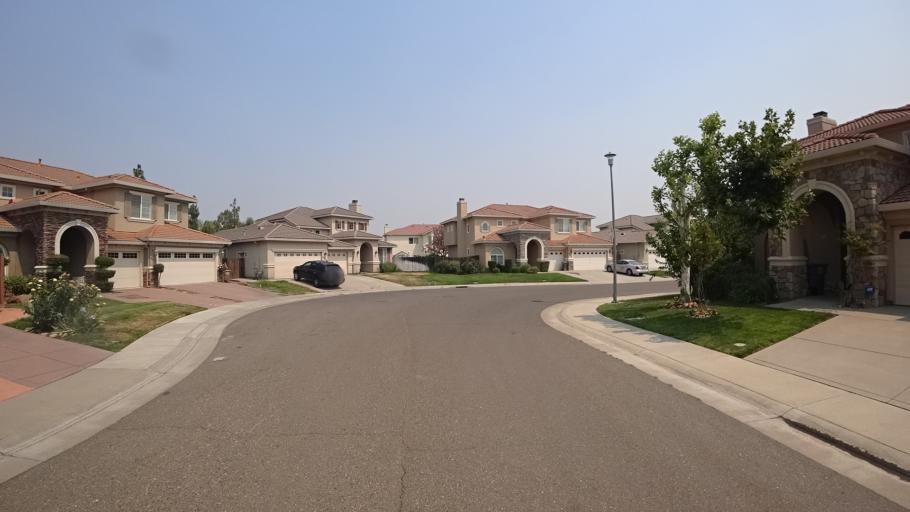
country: US
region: California
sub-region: Sacramento County
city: Laguna
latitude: 38.4027
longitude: -121.4294
